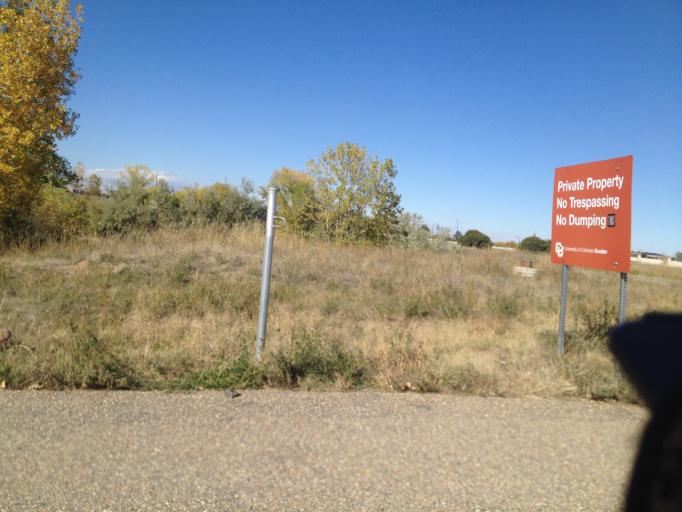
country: US
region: Colorado
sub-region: Boulder County
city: Boulder
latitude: 39.9826
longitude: -105.2317
